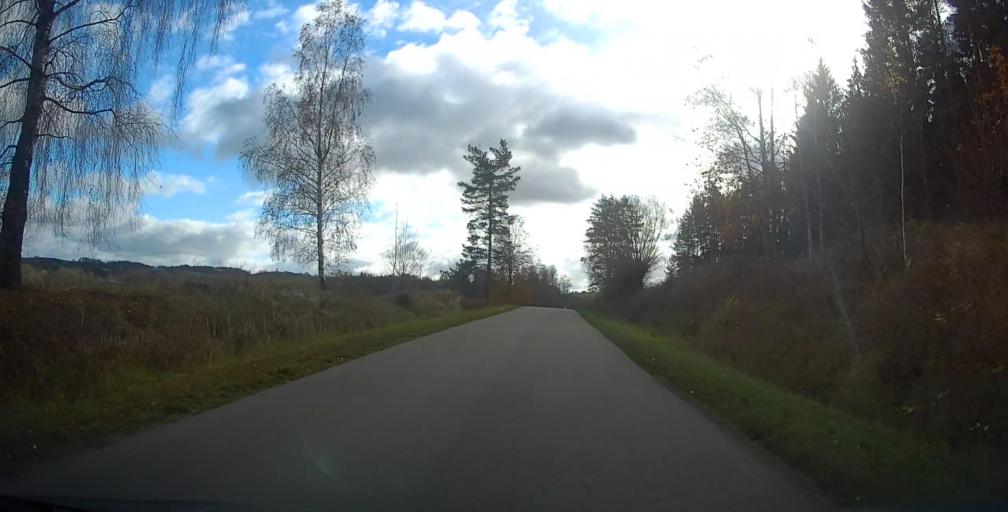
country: PL
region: Podlasie
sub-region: Suwalki
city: Suwalki
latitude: 54.2742
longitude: 22.9084
